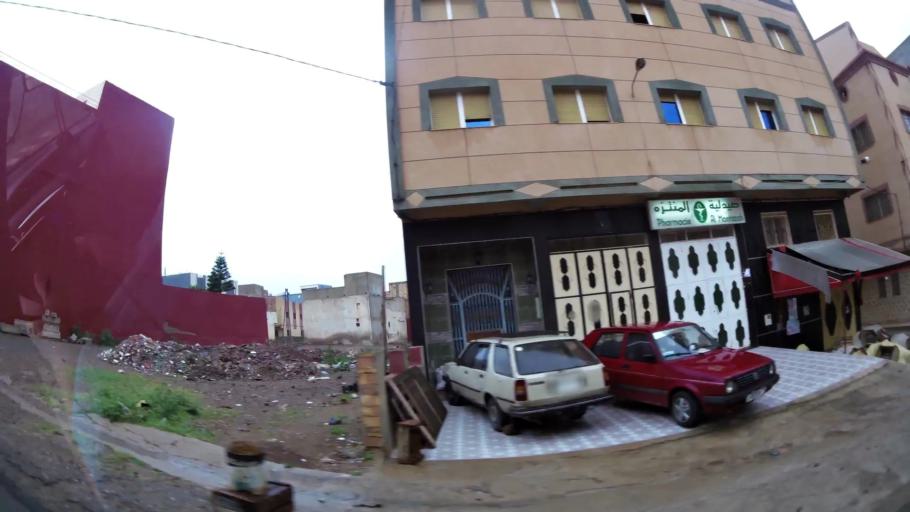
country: MA
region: Oriental
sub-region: Nador
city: Nador
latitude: 35.1840
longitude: -2.9367
